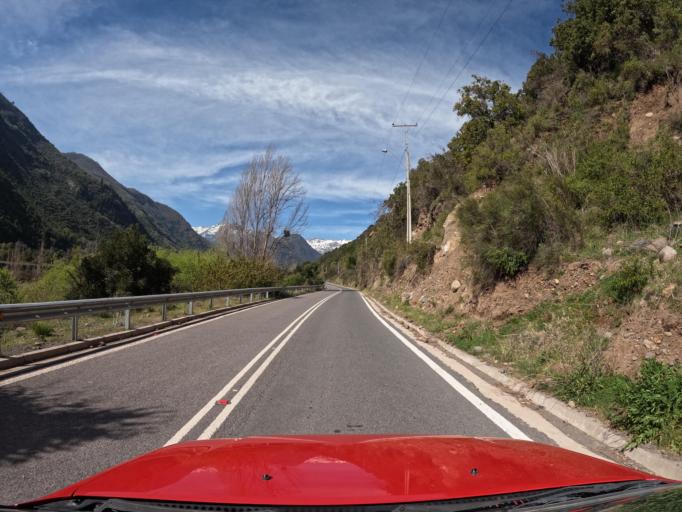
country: CL
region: O'Higgins
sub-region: Provincia de Colchagua
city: Chimbarongo
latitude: -35.0006
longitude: -70.7992
